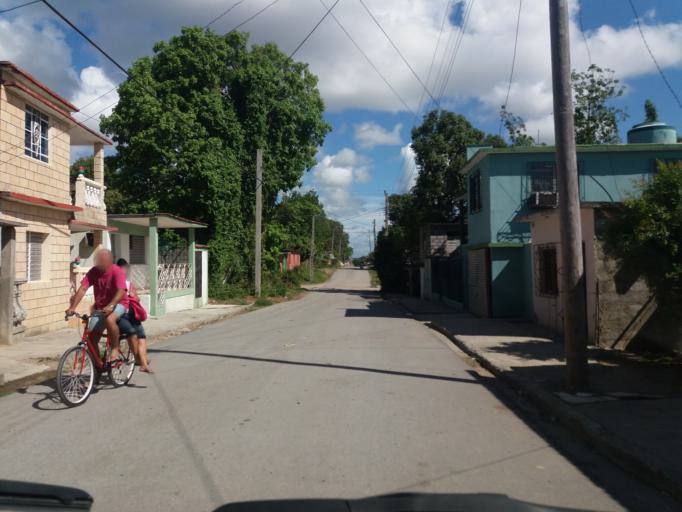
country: CU
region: Cienfuegos
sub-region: Municipio de Cienfuegos
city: Cienfuegos
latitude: 22.1475
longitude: -80.4236
